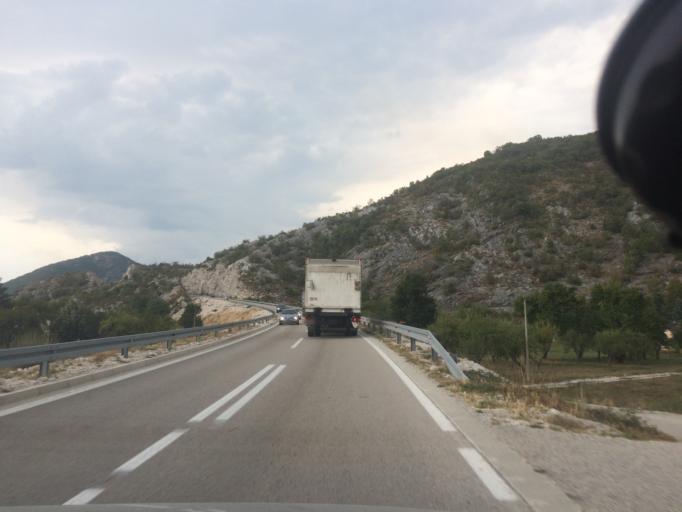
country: ME
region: Kotor
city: Risan
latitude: 42.6536
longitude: 18.6765
